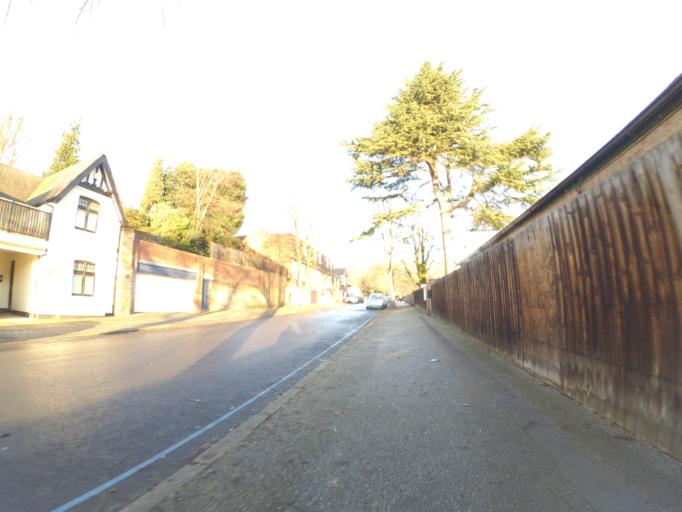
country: GB
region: England
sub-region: Nottingham
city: Nottingham
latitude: 52.9524
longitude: -1.1616
